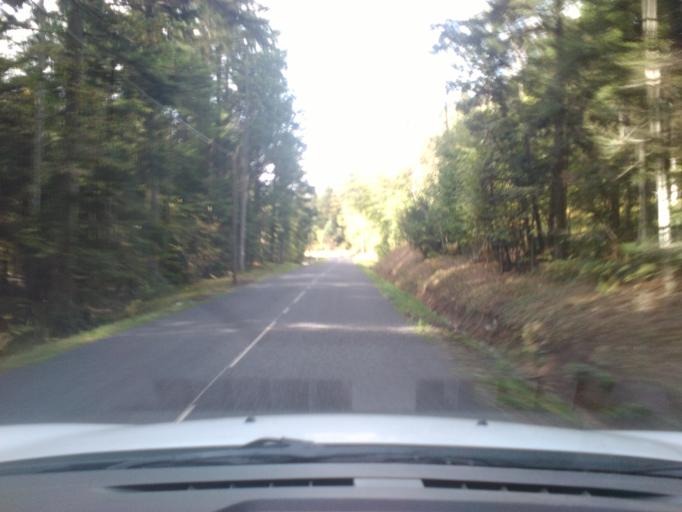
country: FR
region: Lorraine
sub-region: Departement des Vosges
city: Sainte-Marguerite
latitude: 48.2955
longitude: 6.9958
